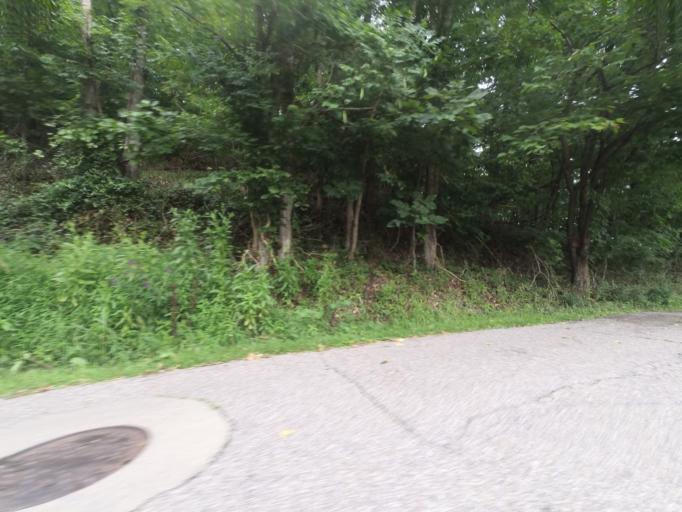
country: US
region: West Virginia
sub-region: Cabell County
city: Huntington
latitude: 38.4016
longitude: -82.4641
